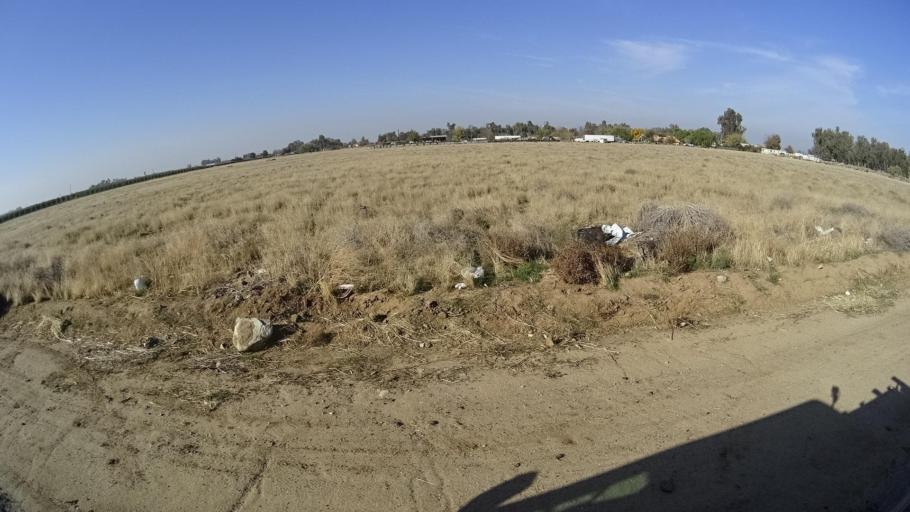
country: US
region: California
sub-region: Kern County
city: Lamont
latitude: 35.3309
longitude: -118.8960
